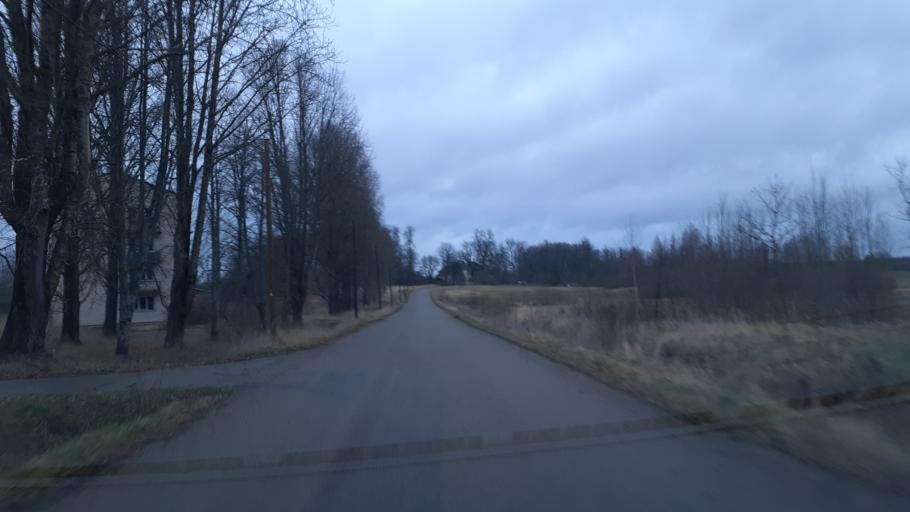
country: LV
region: Kuldigas Rajons
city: Kuldiga
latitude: 57.0400
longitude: 22.1278
